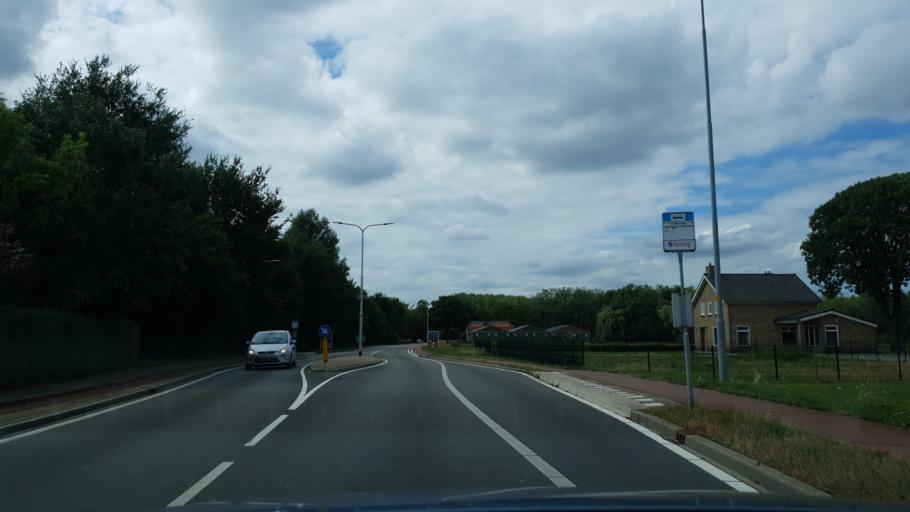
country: NL
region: North Brabant
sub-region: Gemeente Grave
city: Grave
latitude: 51.7660
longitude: 5.7784
